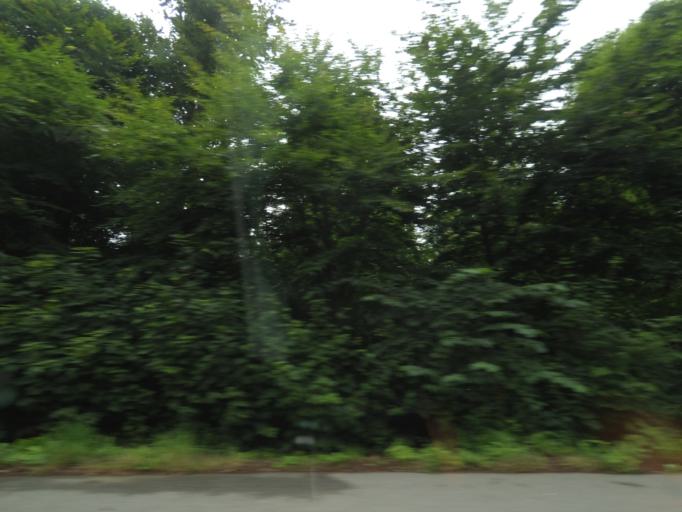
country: DK
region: South Denmark
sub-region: Odense Kommune
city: Odense
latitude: 55.4061
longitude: 10.3680
